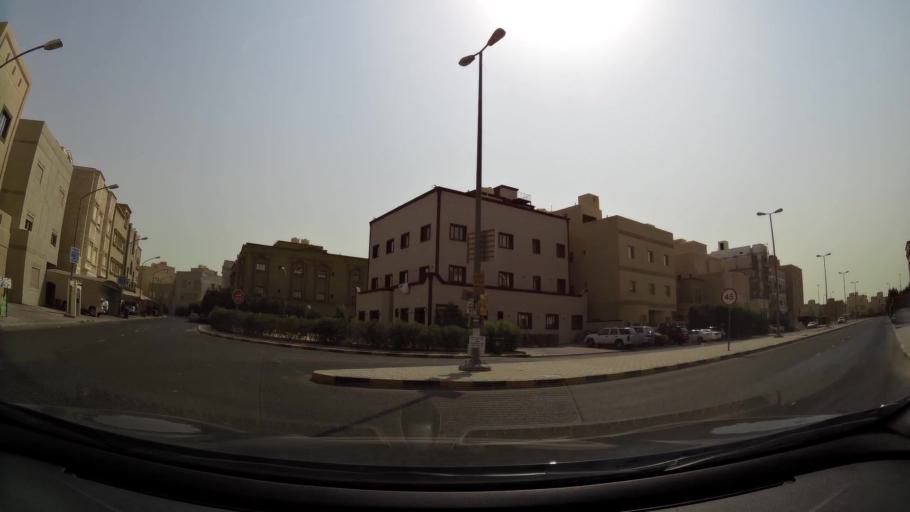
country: KW
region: Muhafazat al Jahra'
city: Al Jahra'
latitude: 29.3216
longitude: 47.7384
